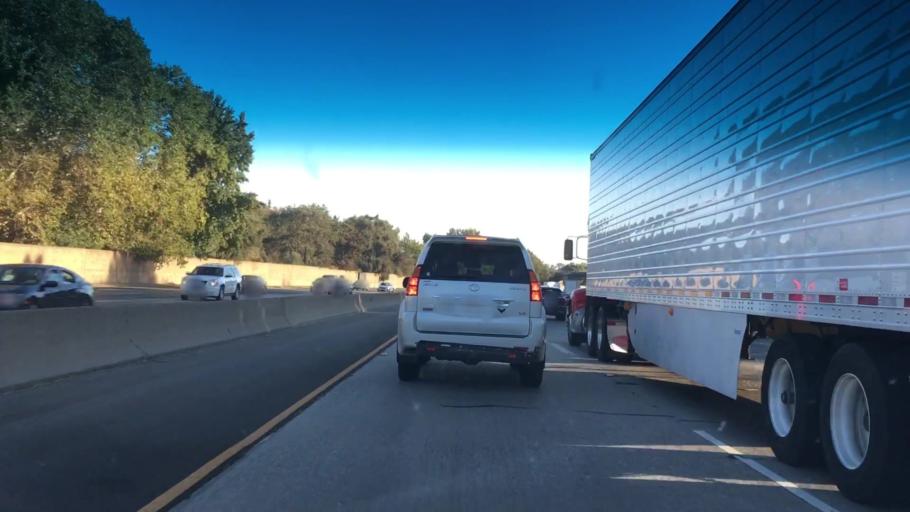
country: US
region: California
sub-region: Sacramento County
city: Sacramento
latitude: 38.5479
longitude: -121.5097
